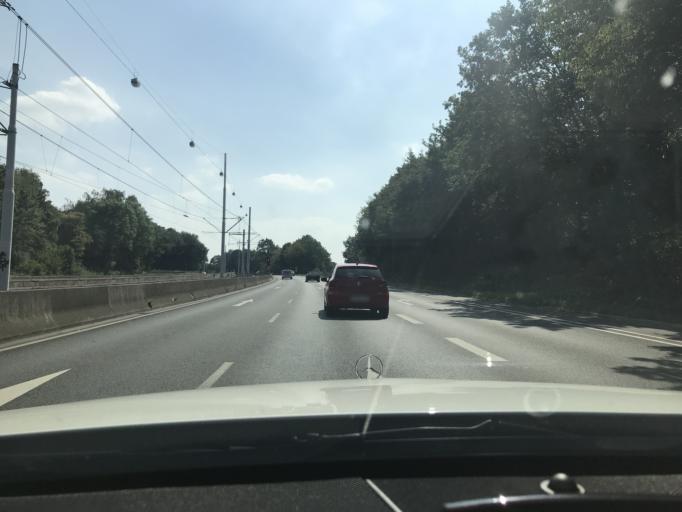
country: DE
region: North Rhine-Westphalia
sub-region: Regierungsbezirk Arnsberg
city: Bochum
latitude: 51.4505
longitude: 7.2476
